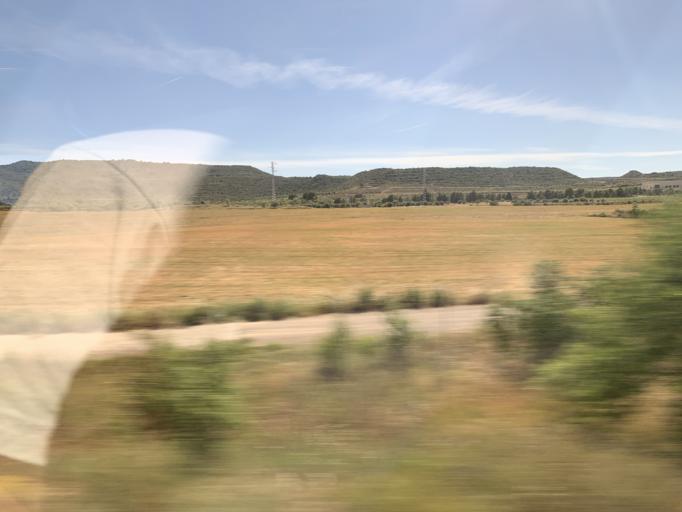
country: ES
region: Catalonia
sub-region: Provincia de Lleida
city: Arbeca
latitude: 41.4840
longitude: 0.8766
